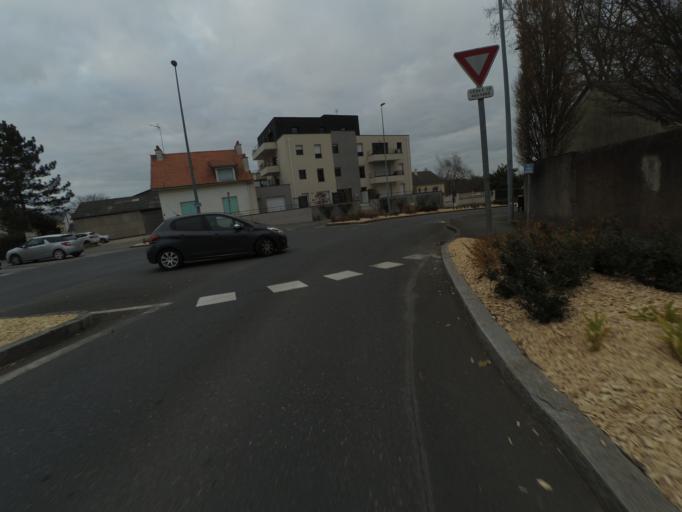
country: FR
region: Pays de la Loire
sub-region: Departement de la Loire-Atlantique
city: Carquefou
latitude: 47.2998
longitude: -1.4892
